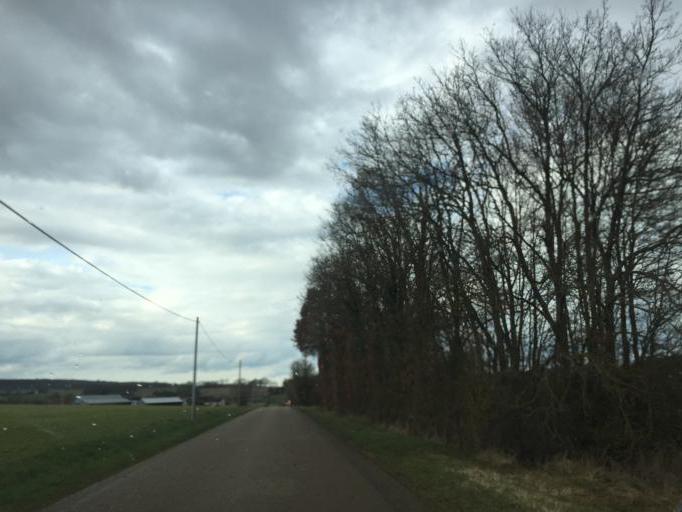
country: FR
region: Bourgogne
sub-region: Departement de l'Yonne
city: Fontenailles
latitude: 47.5538
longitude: 3.3368
